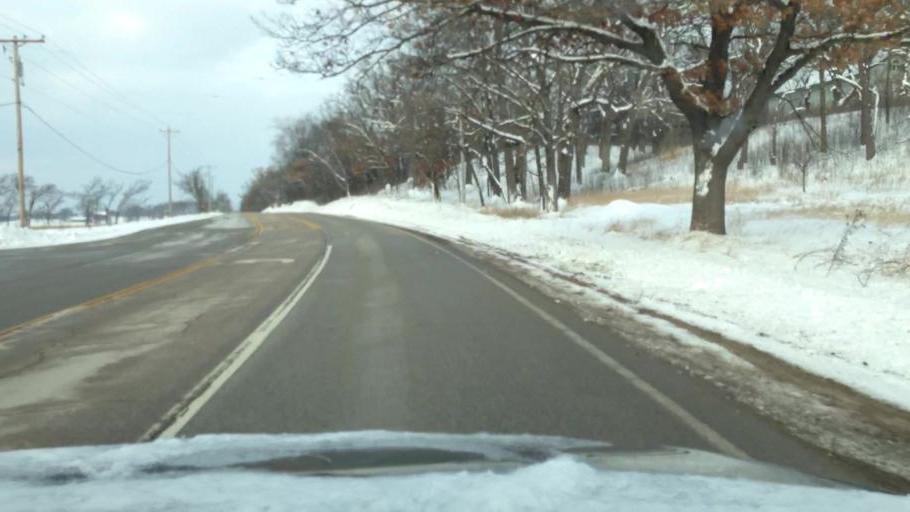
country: US
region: Wisconsin
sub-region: Waukesha County
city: North Prairie
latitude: 42.8898
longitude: -88.4171
